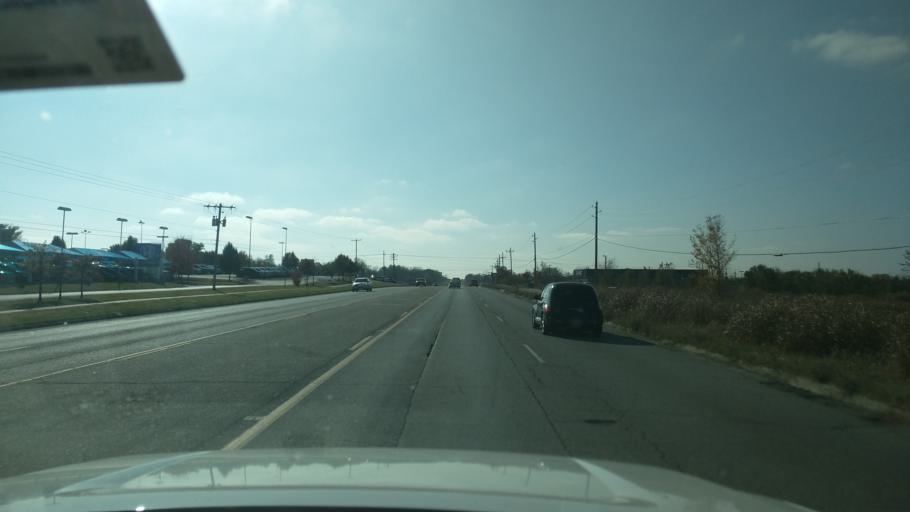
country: US
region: Oklahoma
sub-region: Washington County
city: Bartlesville
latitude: 36.7016
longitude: -95.9352
